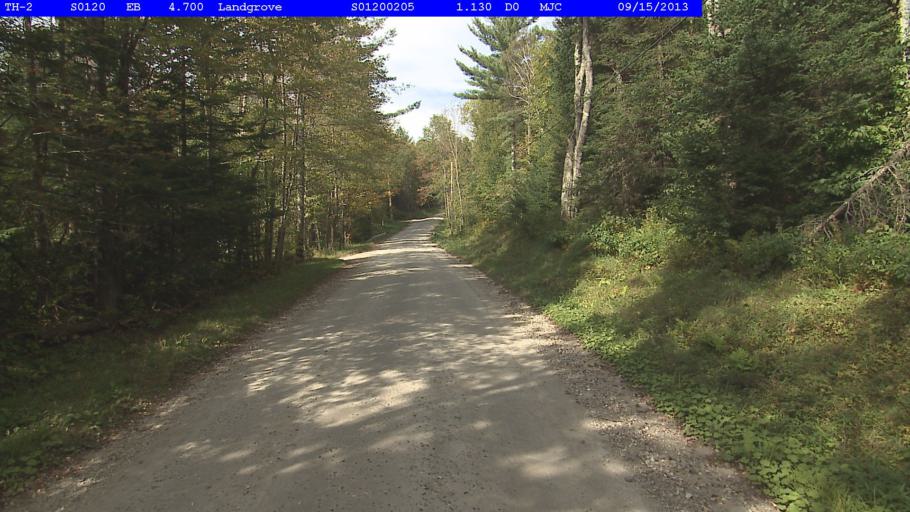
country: US
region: Vermont
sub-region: Bennington County
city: Manchester Center
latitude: 43.2757
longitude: -72.8605
